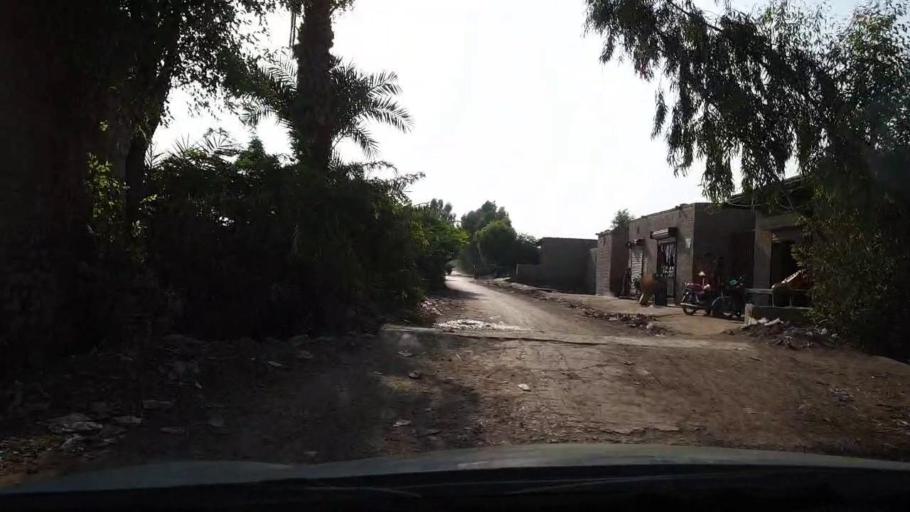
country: PK
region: Sindh
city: Larkana
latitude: 27.5505
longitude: 68.2398
